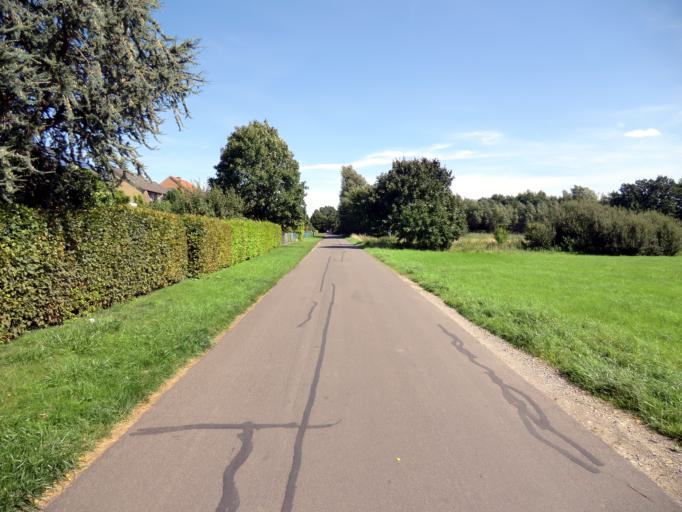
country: DE
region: North Rhine-Westphalia
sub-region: Regierungsbezirk Detmold
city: Herford
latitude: 52.1358
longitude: 8.6463
